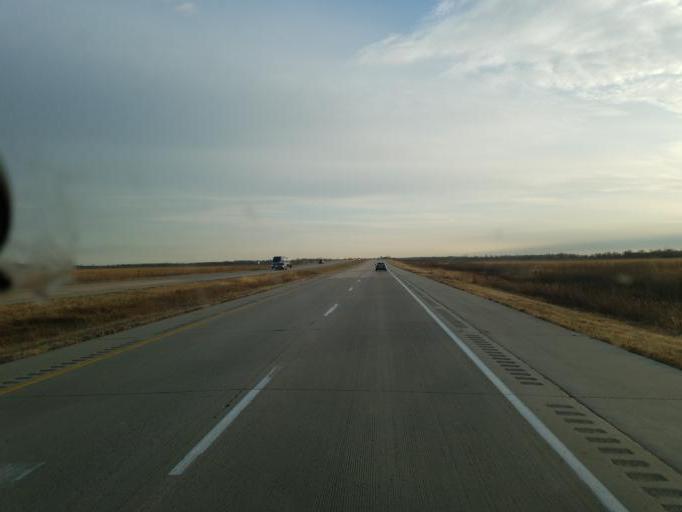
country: US
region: Nebraska
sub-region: Burt County
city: Tekamah
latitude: 41.8704
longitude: -96.1036
